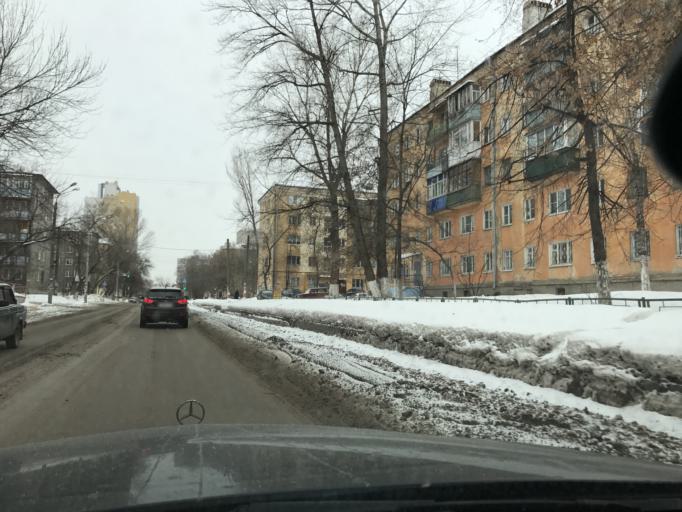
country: RU
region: Nizjnij Novgorod
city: Nizhniy Novgorod
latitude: 56.3306
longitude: 43.9591
